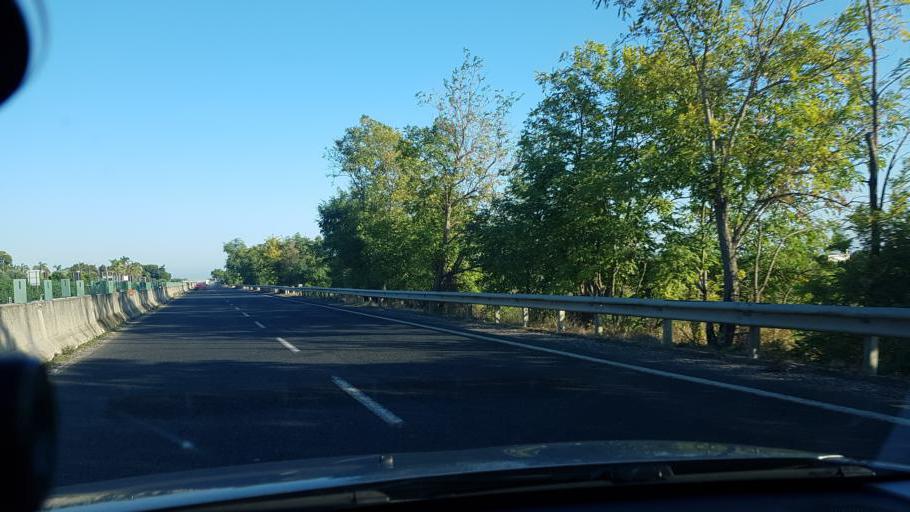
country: IT
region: Apulia
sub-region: Provincia di Bari
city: Monopoli
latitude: 40.8978
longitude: 17.3291
